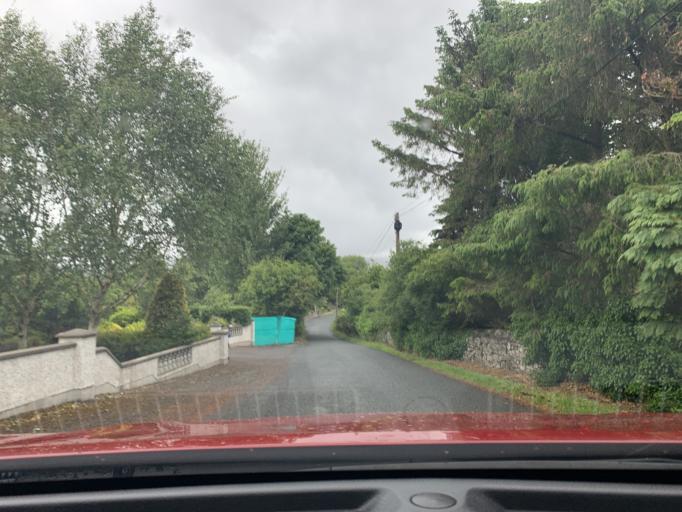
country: IE
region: Connaught
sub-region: Sligo
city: Sligo
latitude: 54.2988
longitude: -8.4592
